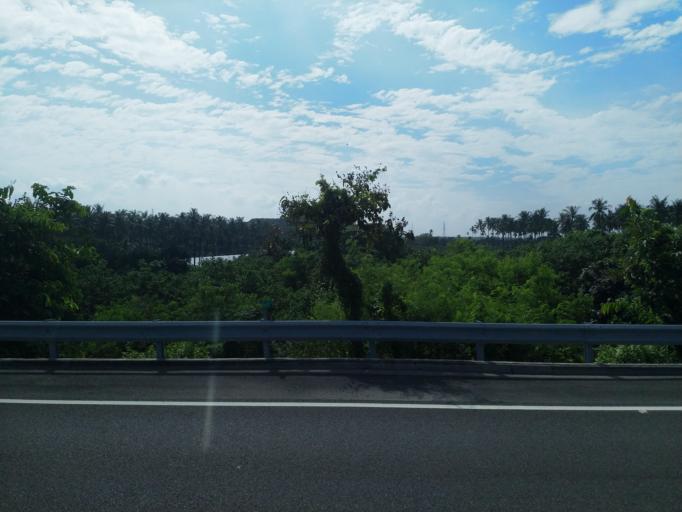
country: TW
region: Taiwan
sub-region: Pingtung
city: Pingtung
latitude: 22.7993
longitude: 120.4730
